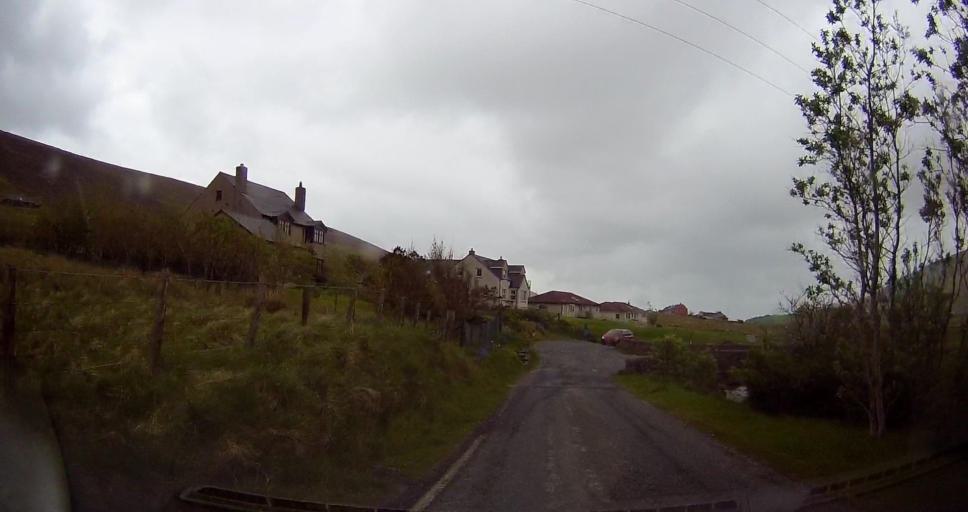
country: GB
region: Scotland
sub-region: Shetland Islands
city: Lerwick
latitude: 60.2553
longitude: -1.2895
